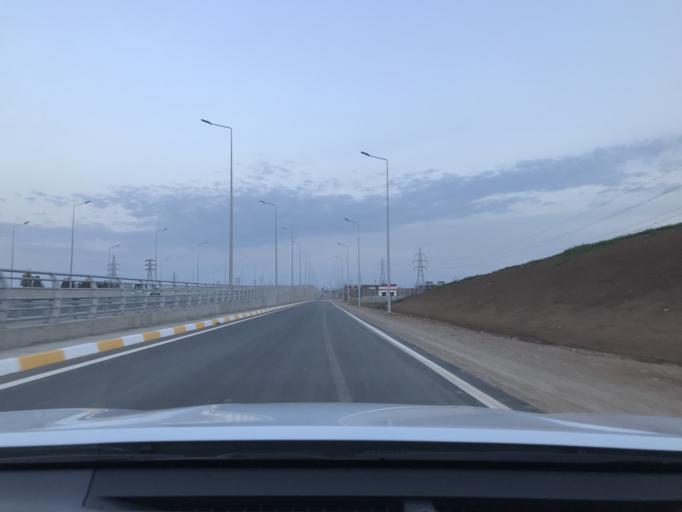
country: IQ
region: Arbil
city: Erbil
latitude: 36.3120
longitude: 43.9133
